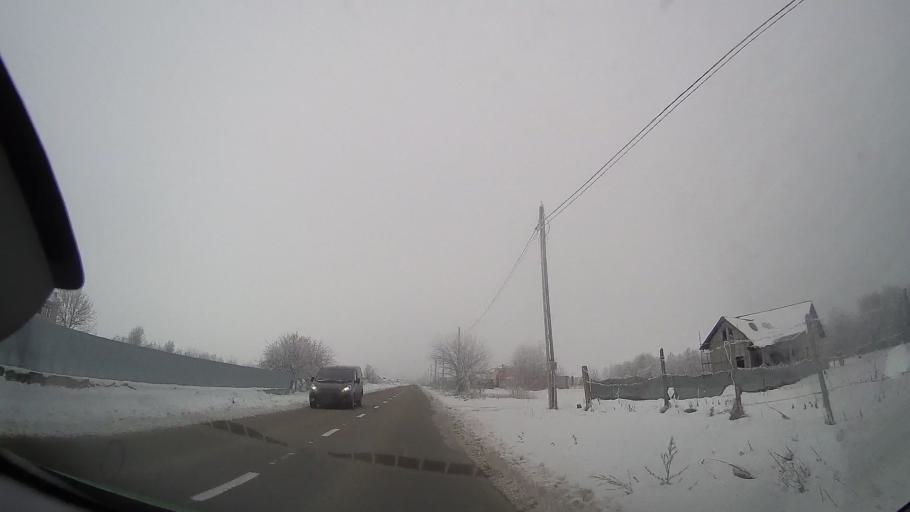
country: RO
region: Neamt
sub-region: Comuna Horia
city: Cotu Vames
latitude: 46.8896
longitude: 26.9659
